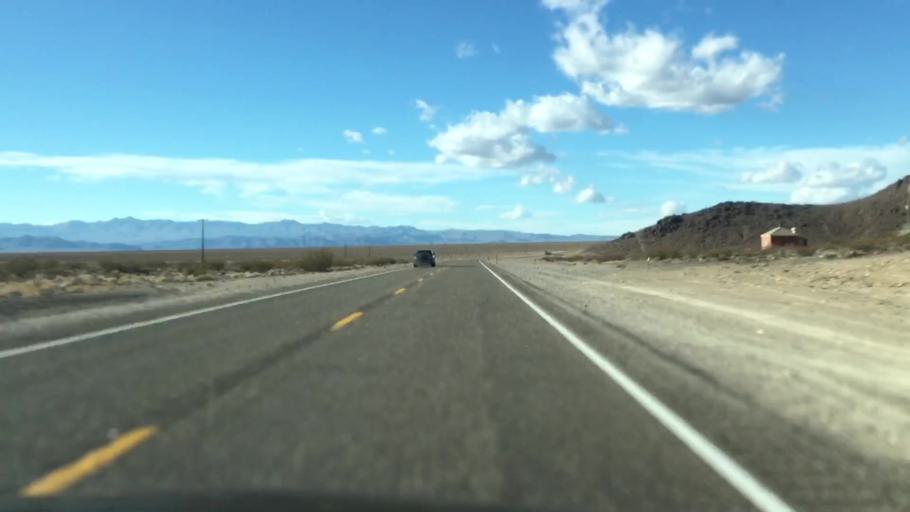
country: US
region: Nevada
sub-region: Nye County
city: Beatty
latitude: 37.1777
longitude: -116.9274
